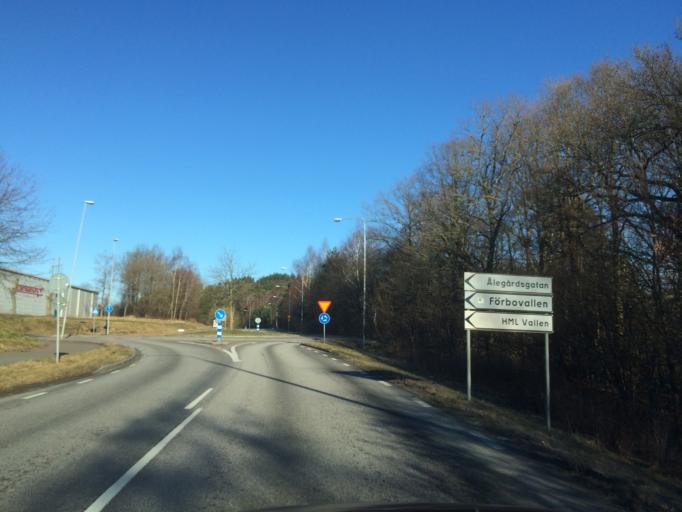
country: SE
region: Vaestra Goetaland
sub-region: Molndal
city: Kallered
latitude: 57.6273
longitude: 12.0326
